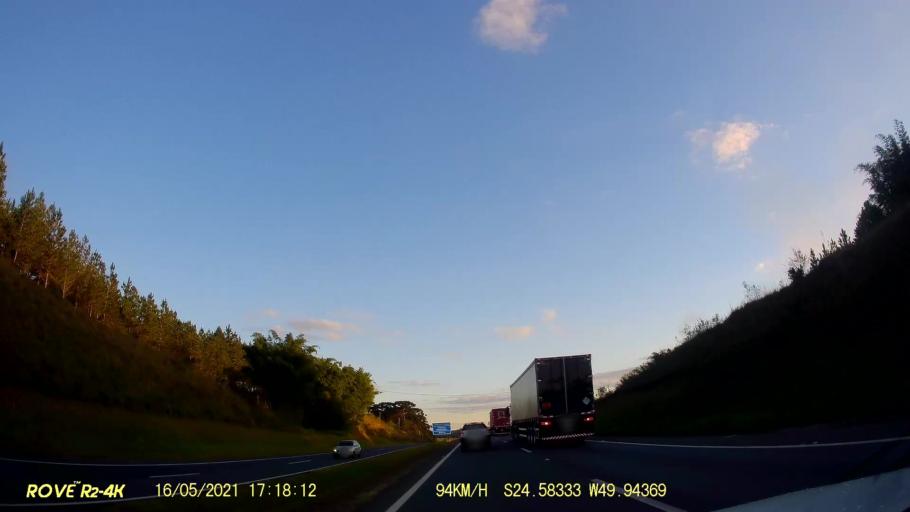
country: BR
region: Parana
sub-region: Pirai Do Sul
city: Pirai do Sul
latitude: -24.5835
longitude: -49.9438
